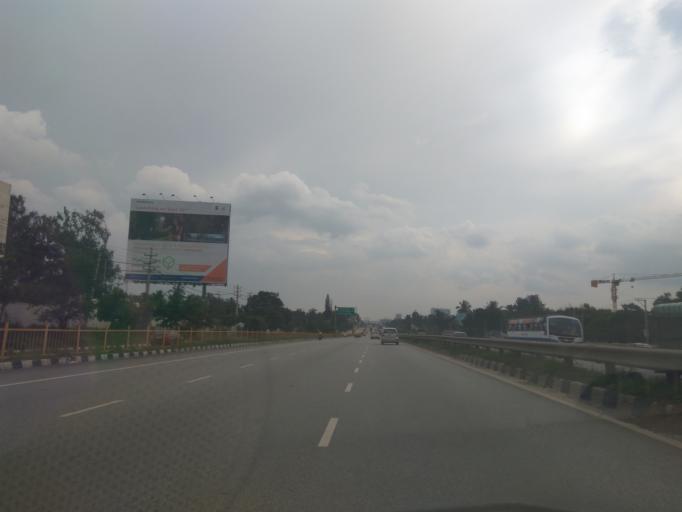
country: IN
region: Karnataka
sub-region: Bangalore Rural
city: Hoskote
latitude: 13.0399
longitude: 77.7418
